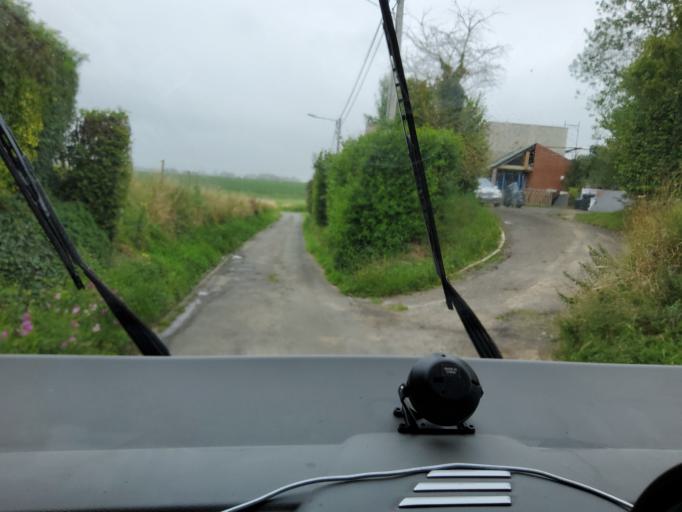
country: BE
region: Wallonia
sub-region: Province du Hainaut
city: Soignies
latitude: 50.6021
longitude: 4.0531
